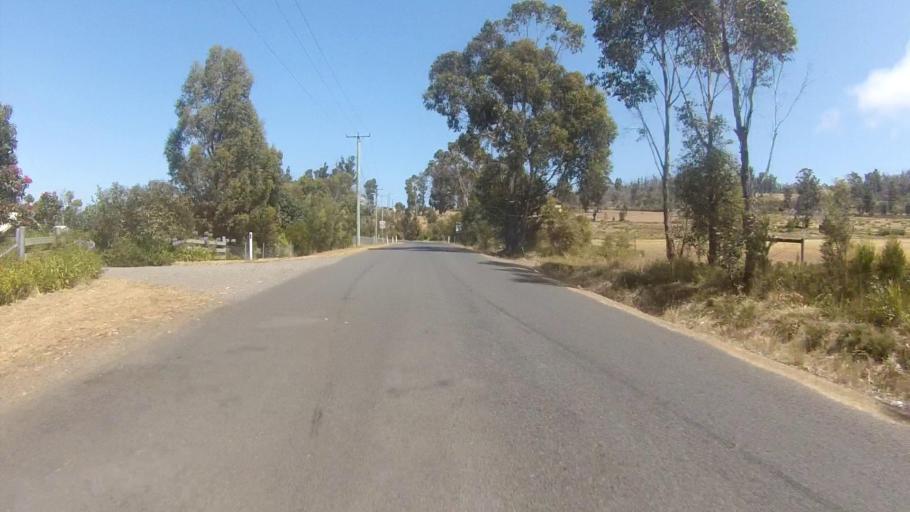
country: AU
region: Tasmania
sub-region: Sorell
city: Sorell
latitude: -42.8699
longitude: 147.8269
